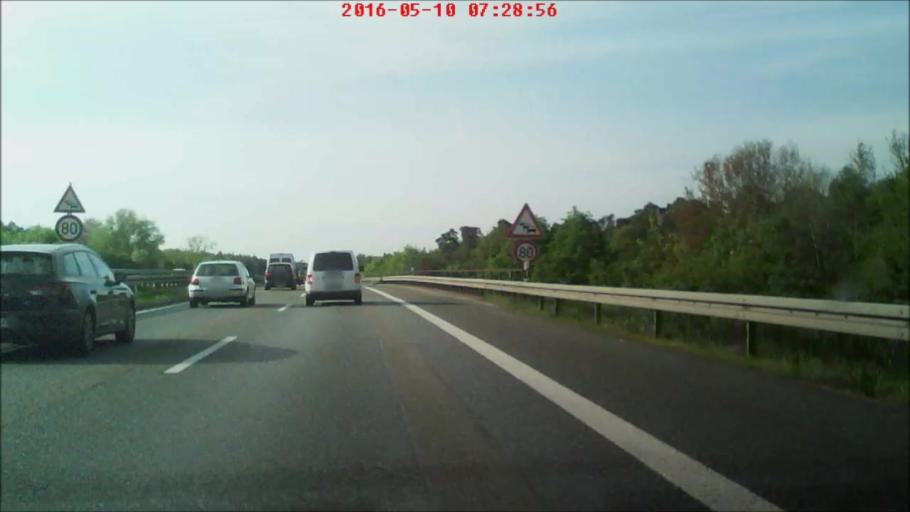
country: DE
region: Hesse
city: Obertshausen
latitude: 50.0714
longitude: 8.8894
